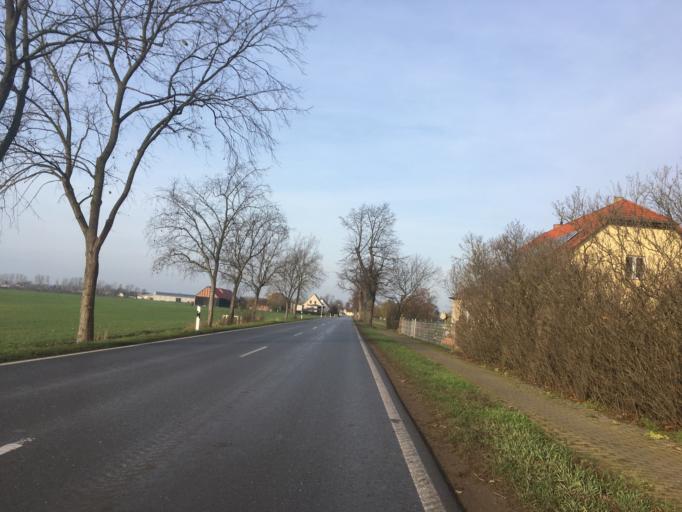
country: DE
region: Brandenburg
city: Wriezen
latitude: 52.7693
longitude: 14.1591
